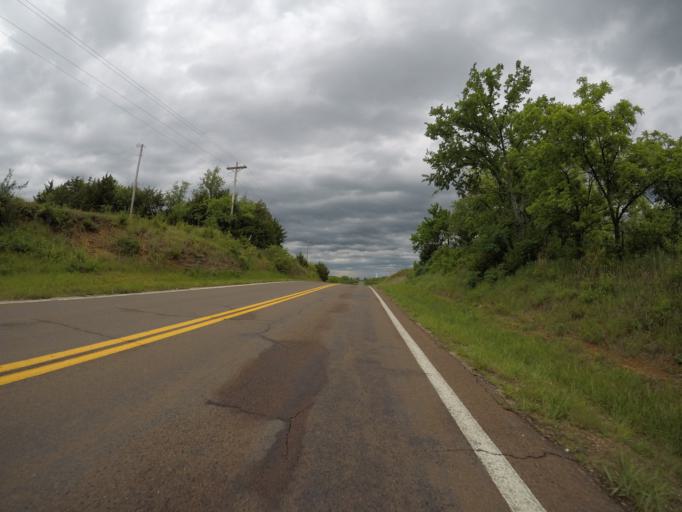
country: US
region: Kansas
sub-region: Shawnee County
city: Auburn
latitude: 38.9645
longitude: -95.9141
